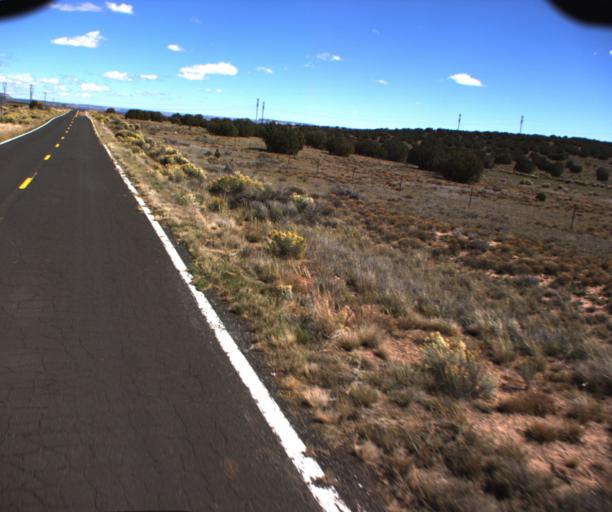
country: US
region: New Mexico
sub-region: McKinley County
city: Zuni Pueblo
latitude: 35.0163
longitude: -109.0550
